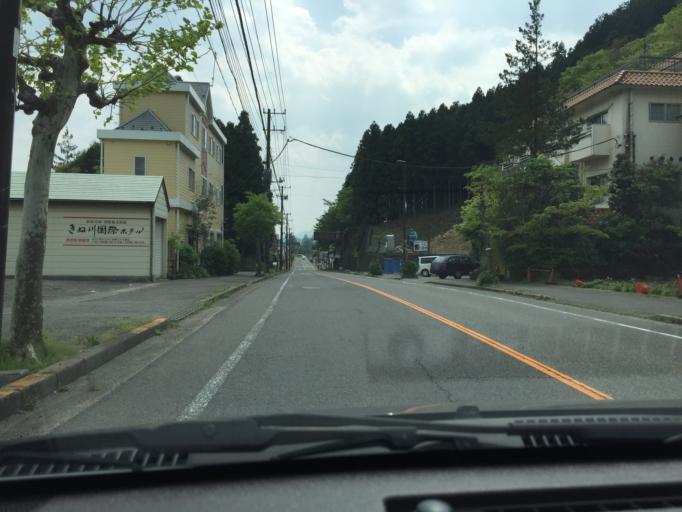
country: JP
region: Tochigi
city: Imaichi
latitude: 36.8344
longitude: 139.7174
